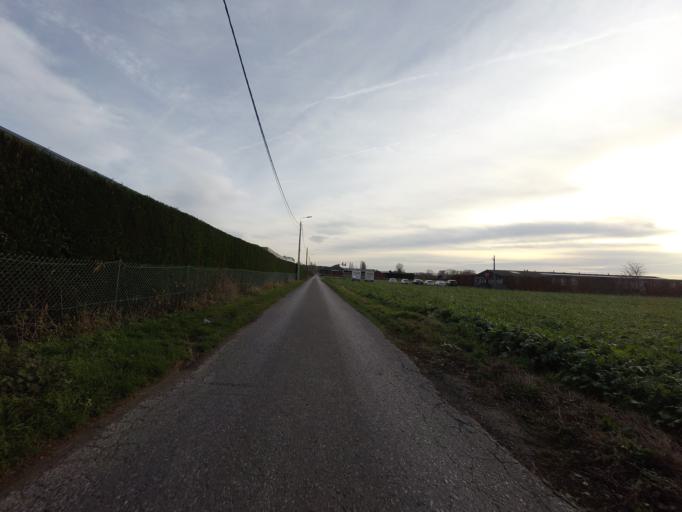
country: BE
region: Flanders
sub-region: Provincie Vlaams-Brabant
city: Kortenberg
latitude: 50.8855
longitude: 4.5179
